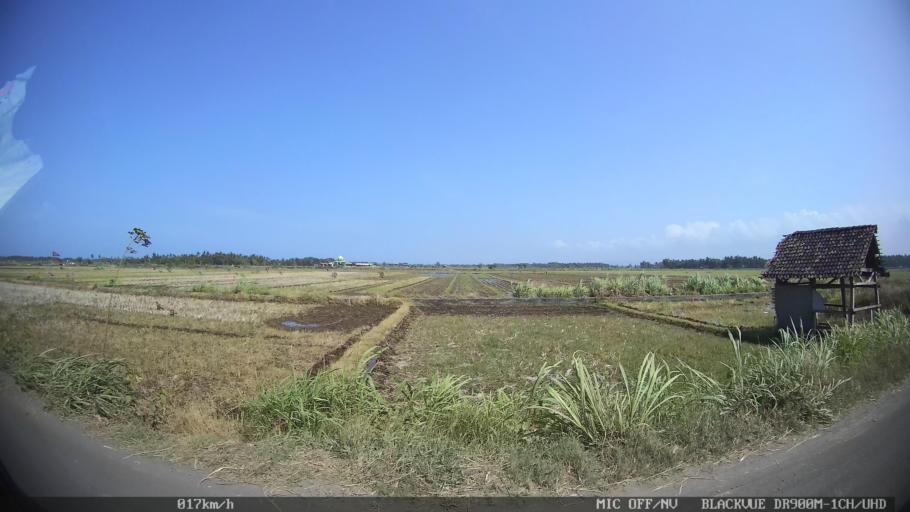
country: ID
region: Daerah Istimewa Yogyakarta
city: Srandakan
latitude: -7.9700
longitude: 110.2114
